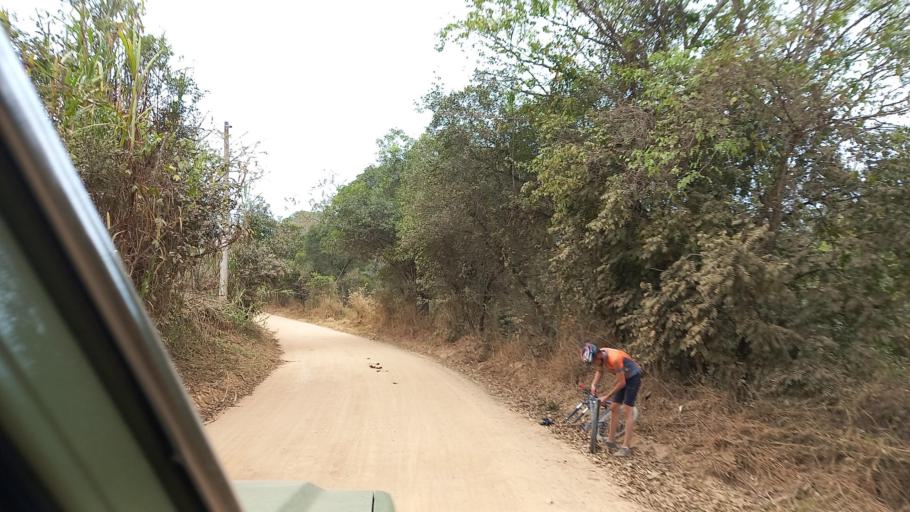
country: BR
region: Sao Paulo
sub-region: Moji-Guacu
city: Mogi-Gaucu
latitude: -22.2994
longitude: -46.8335
